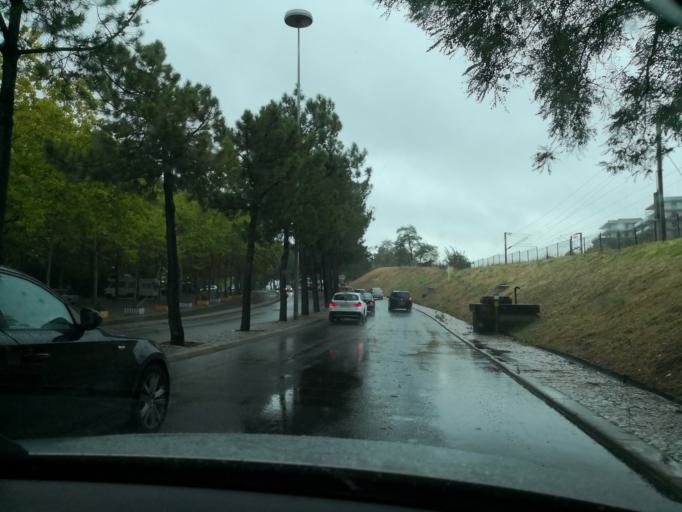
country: PT
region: Lisbon
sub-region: Loures
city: Moscavide
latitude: 38.7831
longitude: -9.1000
